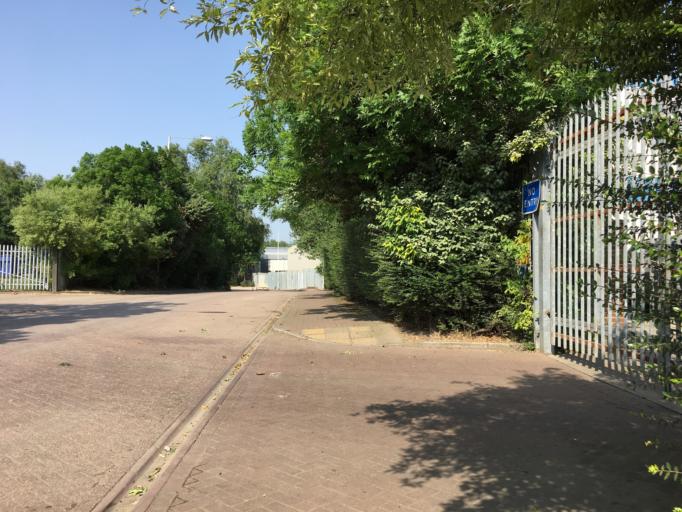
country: GB
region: England
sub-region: Greater London
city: Poplar
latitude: 51.5194
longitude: -0.0015
